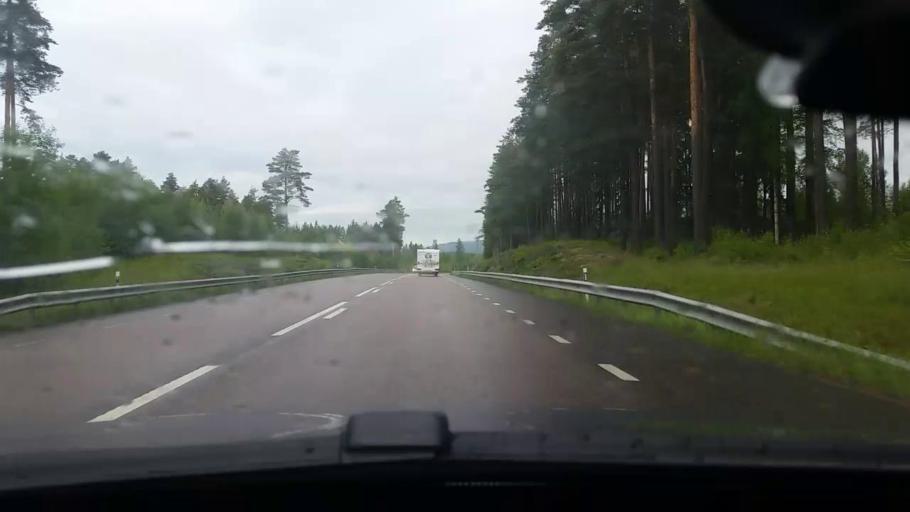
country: SE
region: Dalarna
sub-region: Gagnefs Kommun
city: Gagnef
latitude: 60.6402
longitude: 15.0578
